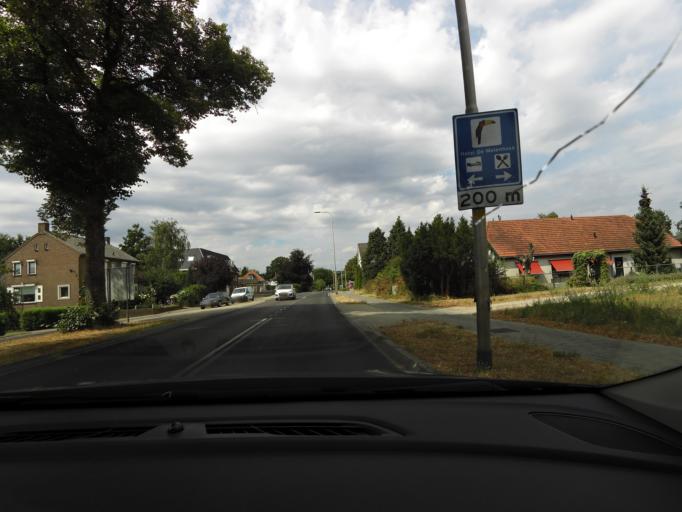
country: NL
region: North Brabant
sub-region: Gemeente Cuijk
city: Cuijk
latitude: 51.7636
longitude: 5.8688
